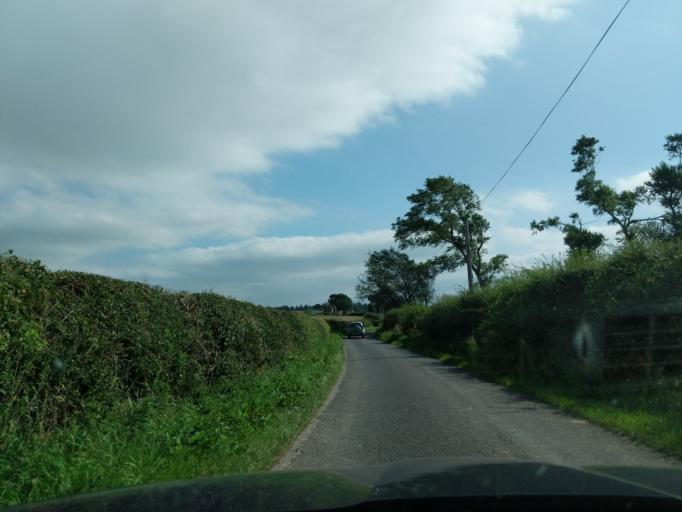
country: GB
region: England
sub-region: Northumberland
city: Ford
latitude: 55.6521
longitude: -2.1450
